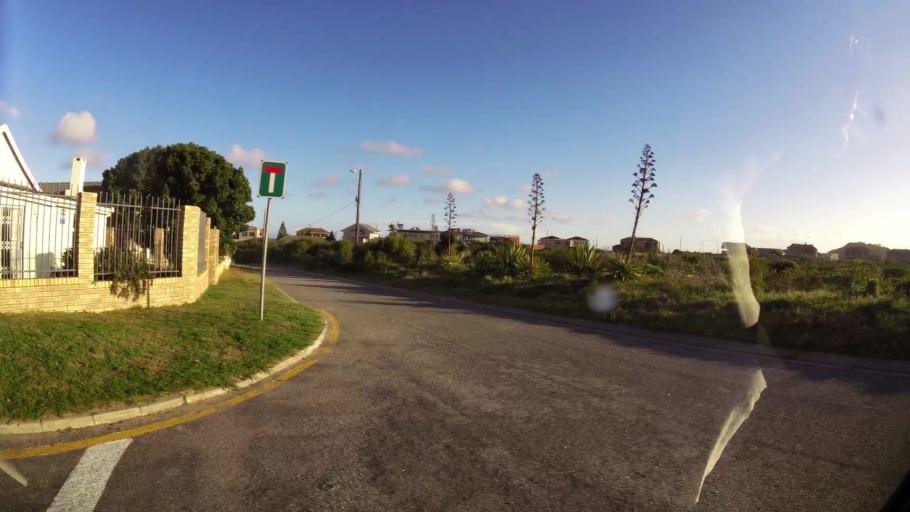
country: ZA
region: Western Cape
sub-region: Eden District Municipality
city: George
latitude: -34.0029
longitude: 22.6542
